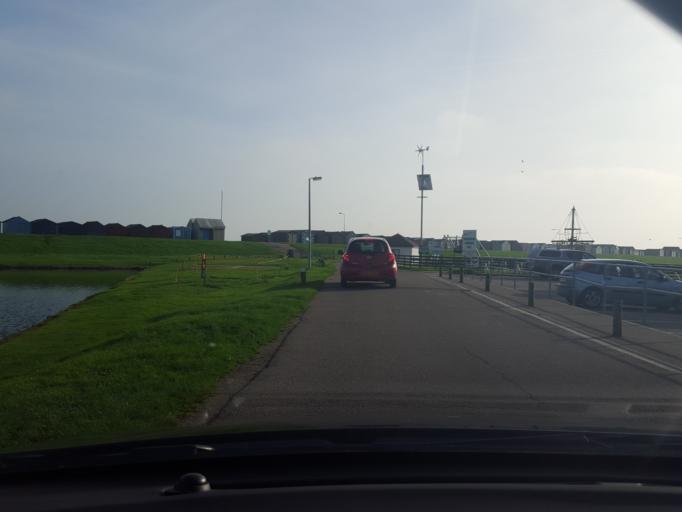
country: GB
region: England
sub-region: Essex
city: Dovercourt
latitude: 51.9274
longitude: 1.2705
